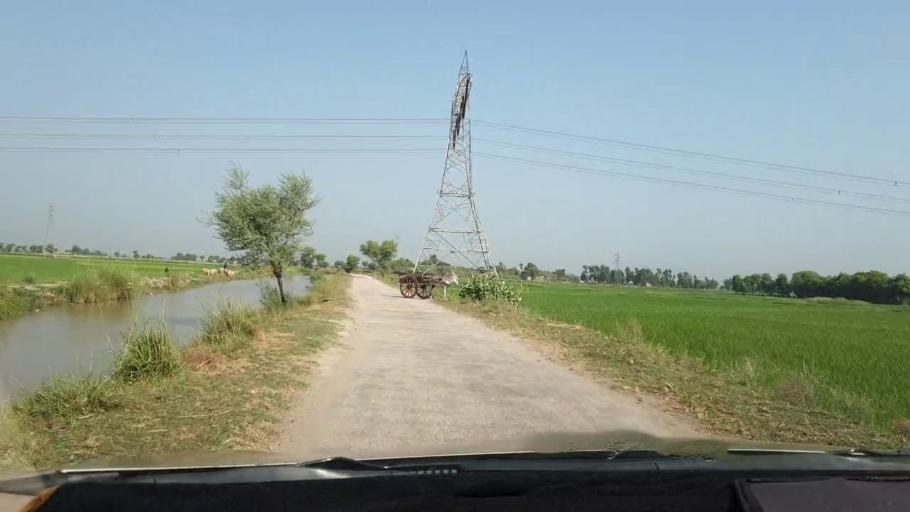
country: PK
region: Sindh
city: Larkana
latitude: 27.6380
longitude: 68.2362
